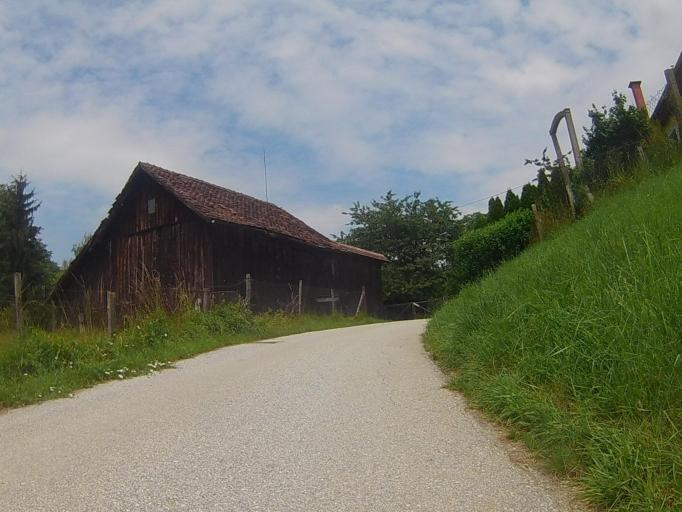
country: SI
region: Maribor
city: Maribor
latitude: 46.5747
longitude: 15.6458
